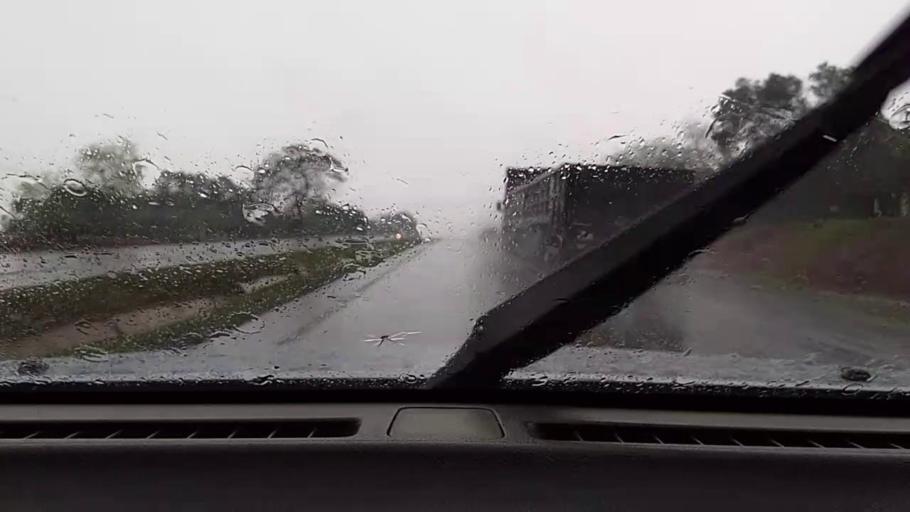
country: PY
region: Caaguazu
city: Repatriacion
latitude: -25.4456
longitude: -55.8845
